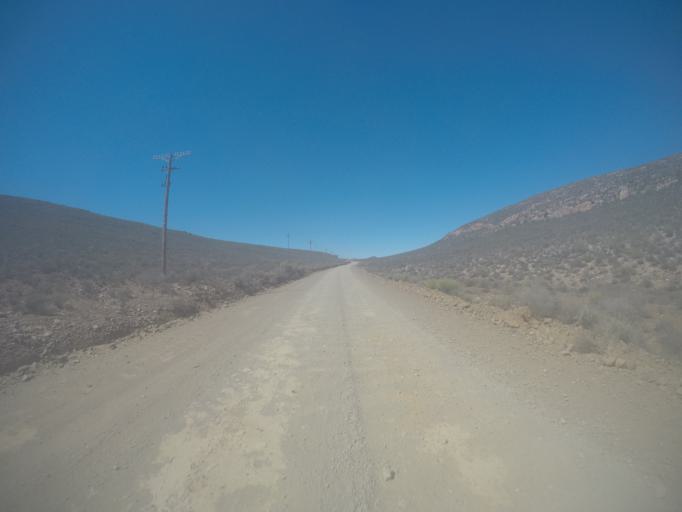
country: ZA
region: Western Cape
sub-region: West Coast District Municipality
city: Clanwilliam
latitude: -32.5258
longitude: 19.3524
